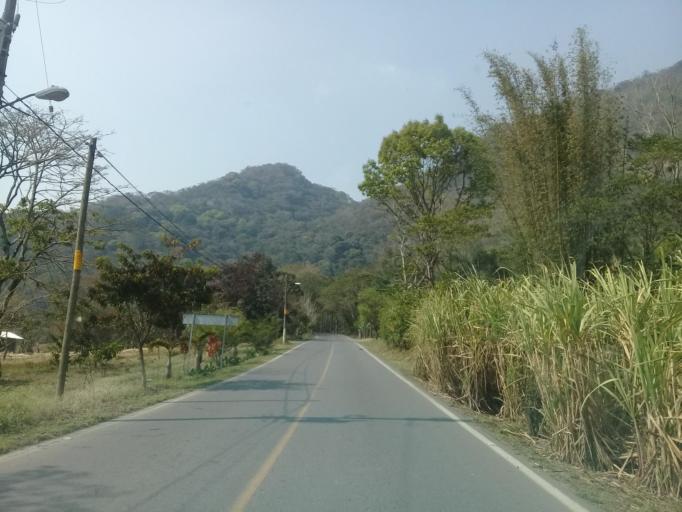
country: MX
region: Veracruz
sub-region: Ixtaczoquitlan
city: Campo Chico
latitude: 18.8373
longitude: -97.0227
